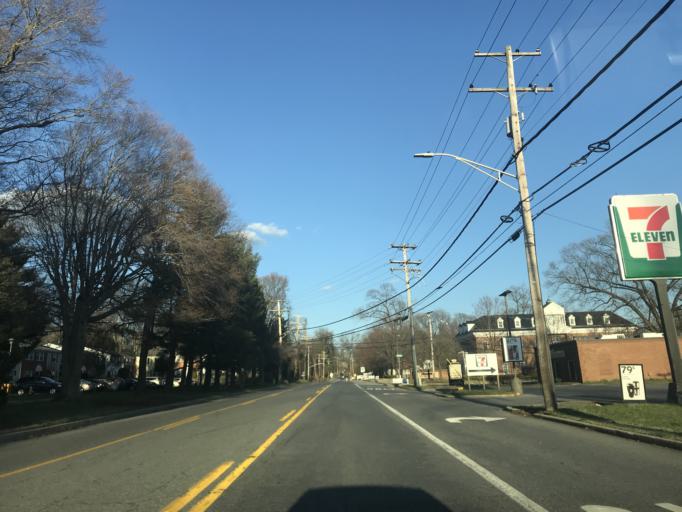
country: US
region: Maryland
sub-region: Anne Arundel County
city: Crofton
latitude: 38.9920
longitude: -76.6960
